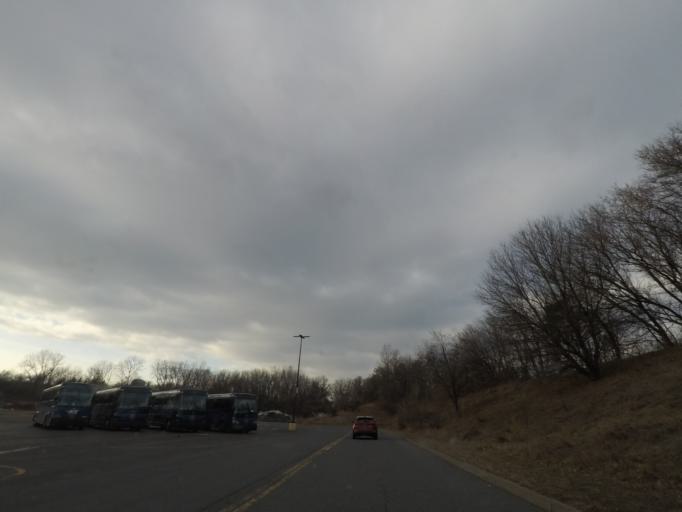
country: US
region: New York
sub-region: Albany County
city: McKownville
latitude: 42.6929
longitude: -73.8541
